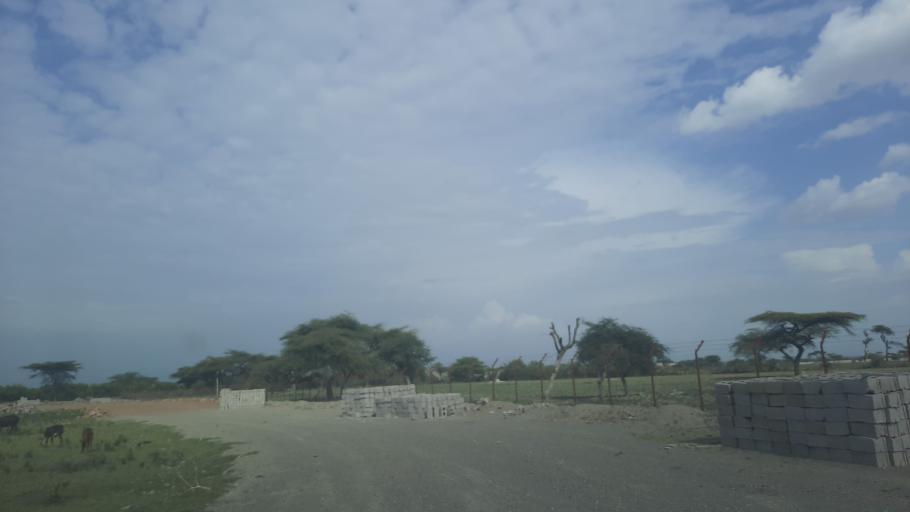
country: ET
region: Oromiya
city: Ziway
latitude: 7.6976
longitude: 38.6557
